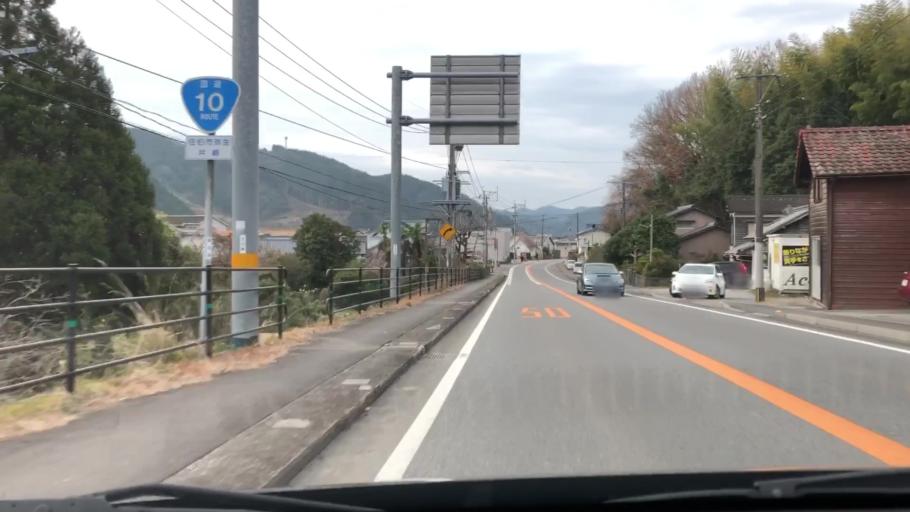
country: JP
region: Oita
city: Saiki
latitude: 32.9796
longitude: 131.8469
